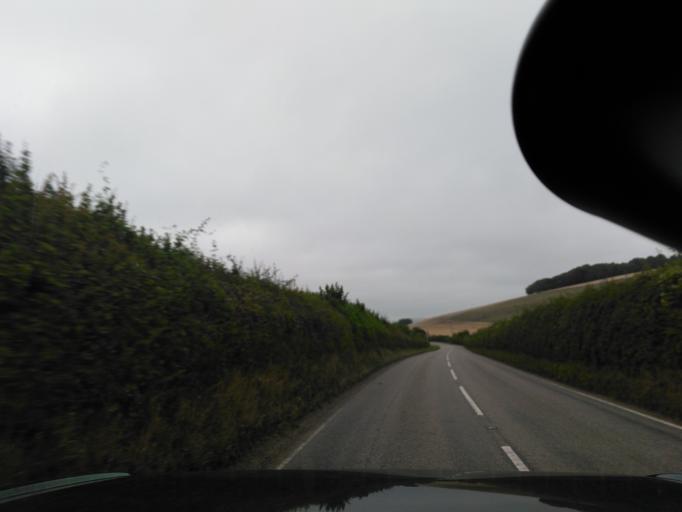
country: GB
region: England
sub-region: Dorset
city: Blandford Forum
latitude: 50.9142
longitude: -2.1956
